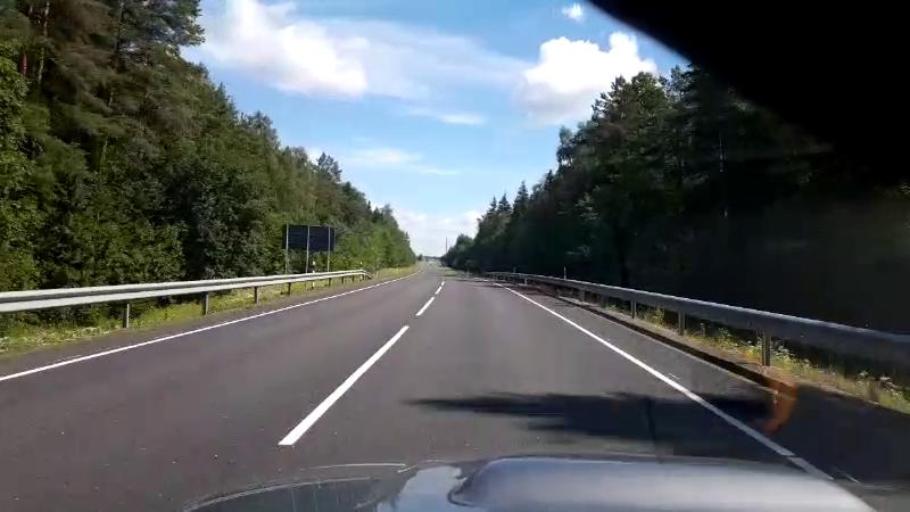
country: EE
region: Jaervamaa
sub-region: Jaerva-Jaani vald
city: Jarva-Jaani
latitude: 59.1298
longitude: 25.7503
